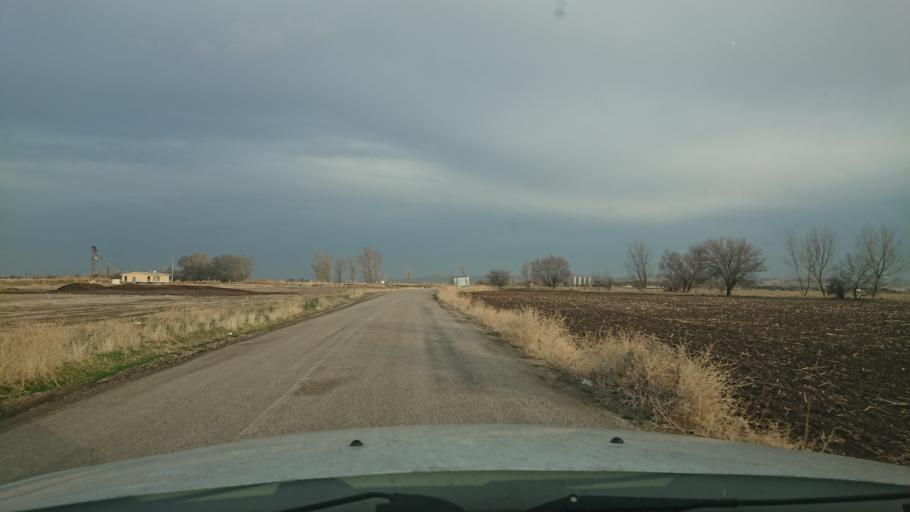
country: TR
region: Aksaray
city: Yesilova
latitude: 38.4449
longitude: 33.8367
